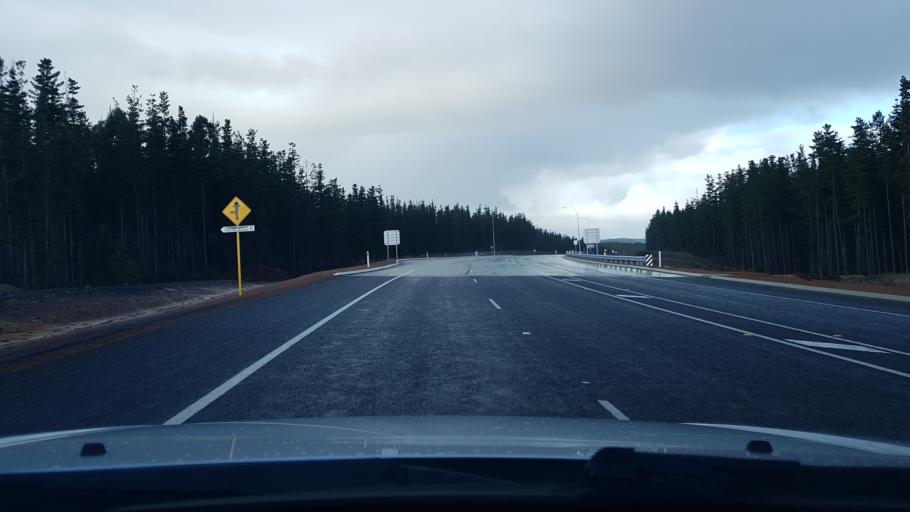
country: AU
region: Western Australia
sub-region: Augusta-Margaret River Shire
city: Margaret River
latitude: -33.9344
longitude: 115.0877
